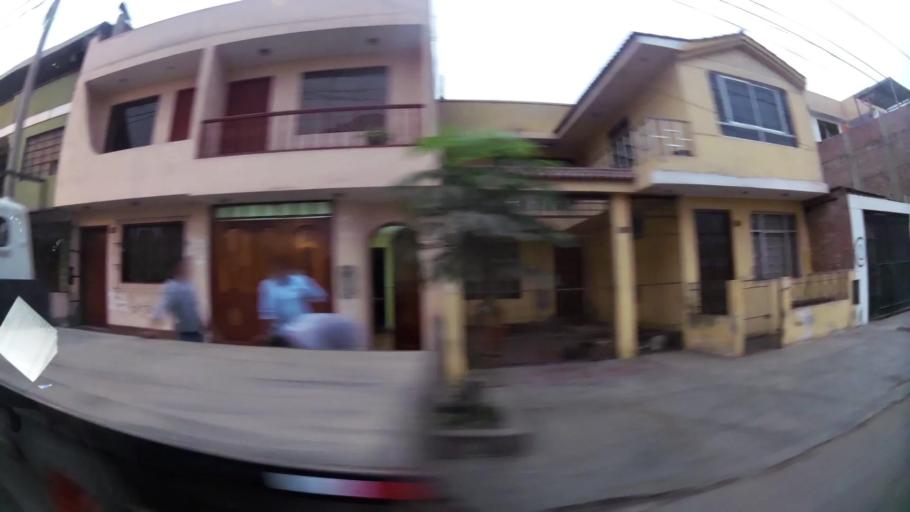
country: PE
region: Lima
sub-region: Lima
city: Surco
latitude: -12.1660
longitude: -76.9708
